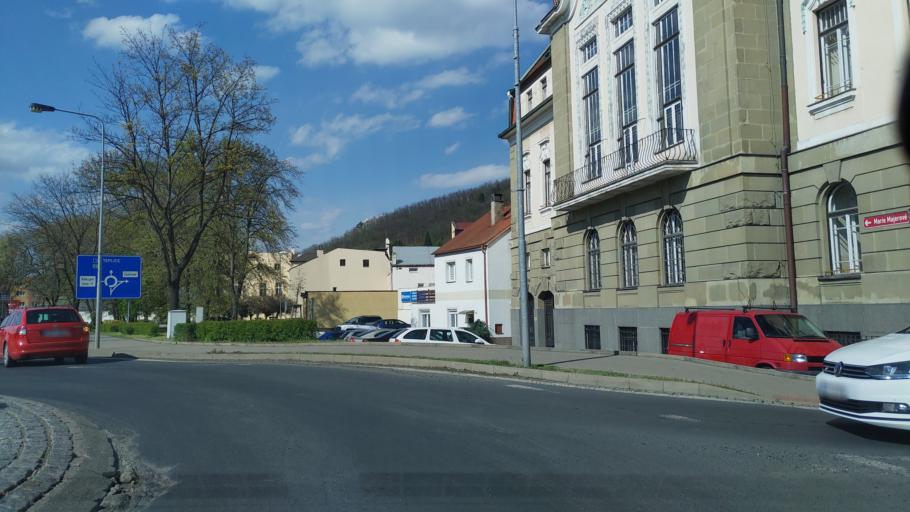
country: CZ
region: Ustecky
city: Bilina
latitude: 50.5488
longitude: 13.7738
